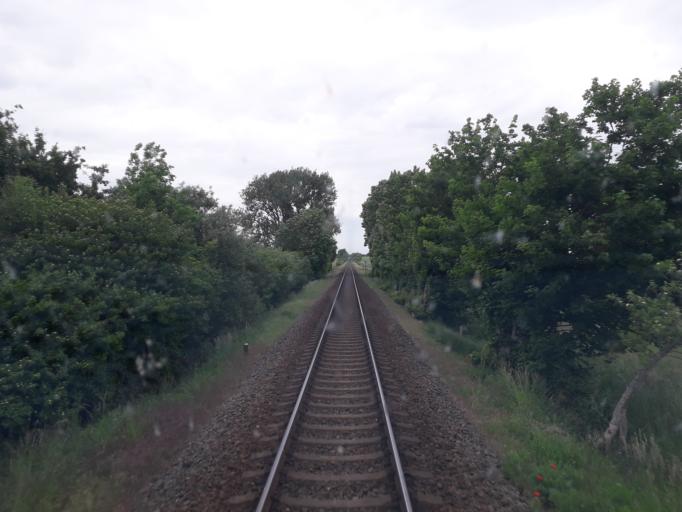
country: DE
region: Brandenburg
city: Neuruppin
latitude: 52.9066
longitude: 12.8441
